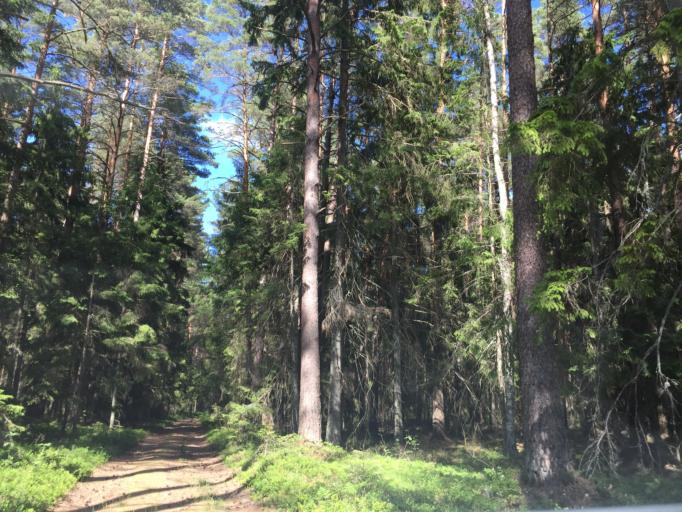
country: LV
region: Ventspils
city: Ventspils
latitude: 57.4747
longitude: 21.6577
